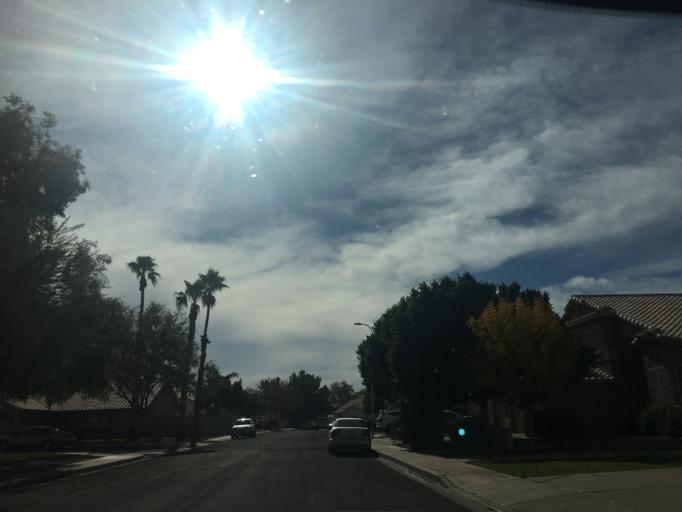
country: US
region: Arizona
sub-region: Maricopa County
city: Gilbert
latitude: 33.3468
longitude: -111.8109
